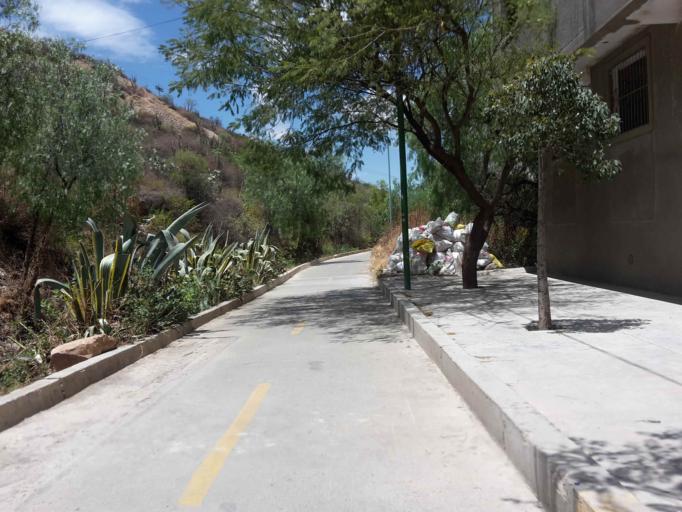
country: BO
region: Cochabamba
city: Cochabamba
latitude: -17.3847
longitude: -66.1410
